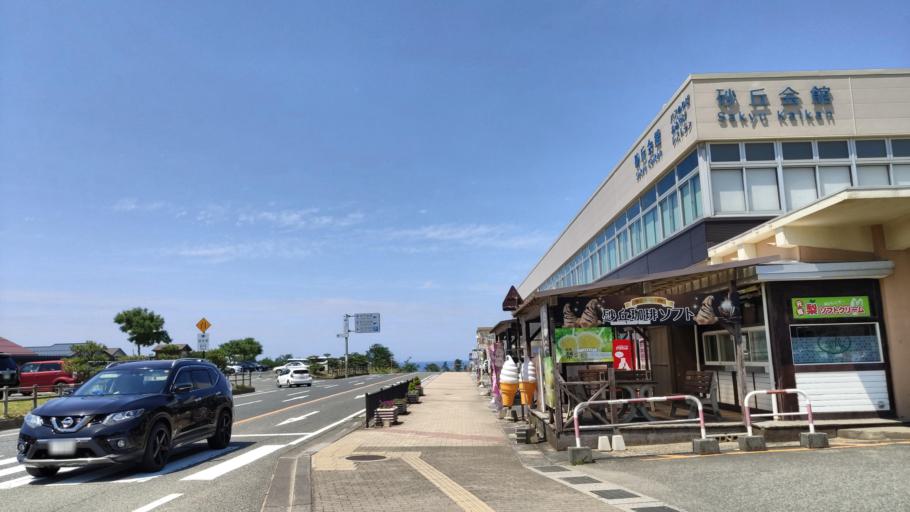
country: JP
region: Tottori
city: Tottori
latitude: 35.5434
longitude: 134.2371
